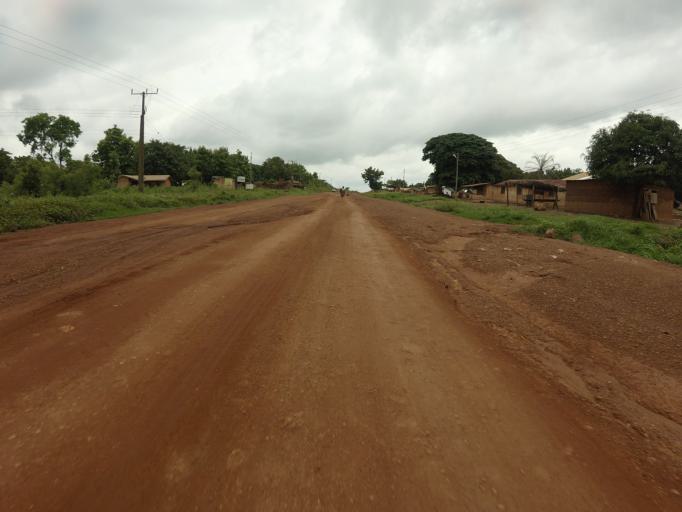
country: GH
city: Kpandae
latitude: 8.3131
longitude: 0.4813
